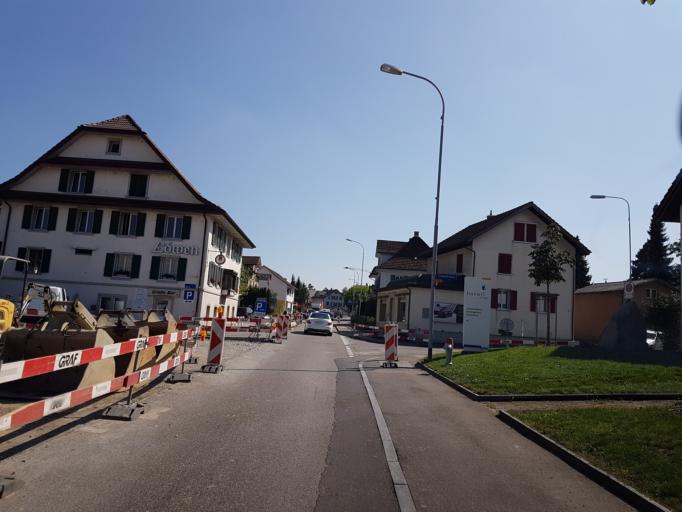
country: CH
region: Aargau
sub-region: Bezirk Muri
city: Buttwil
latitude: 47.3022
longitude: 8.3125
